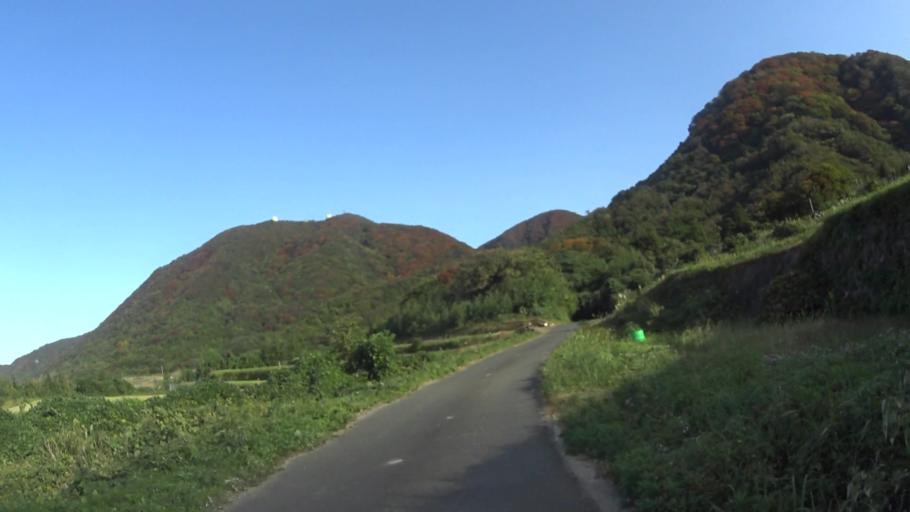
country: JP
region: Kyoto
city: Miyazu
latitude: 35.7613
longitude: 135.2030
